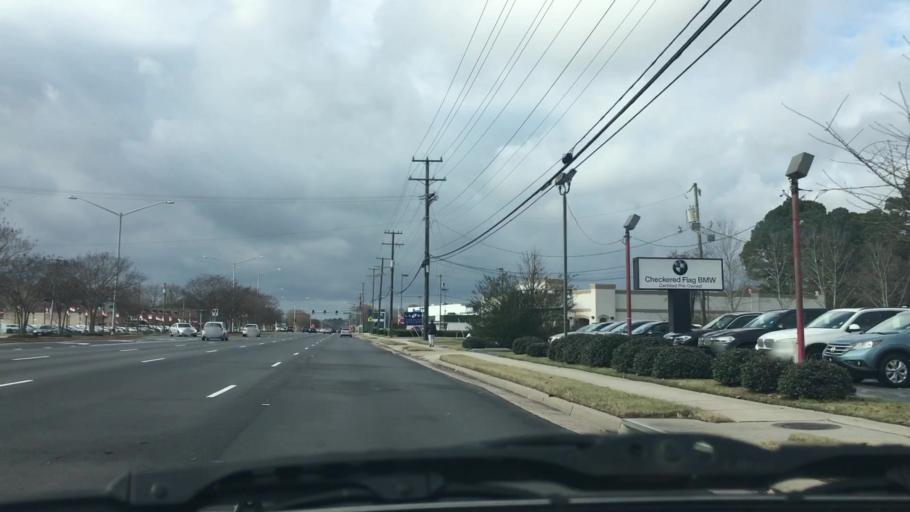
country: US
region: Virginia
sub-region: City of Chesapeake
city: Chesapeake
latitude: 36.8479
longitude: -76.1617
